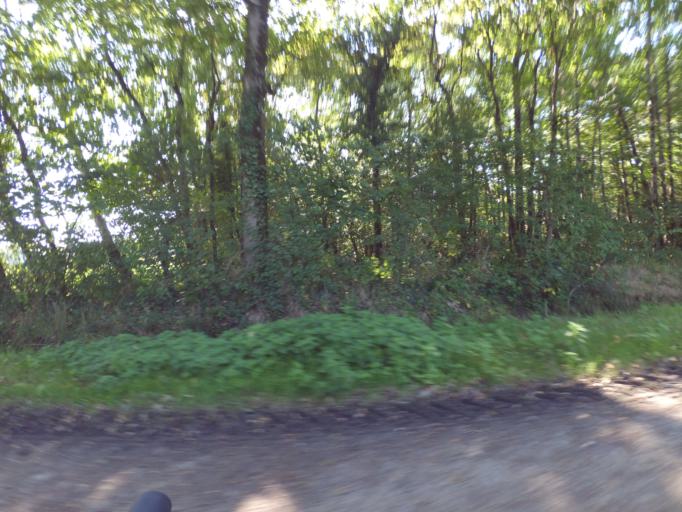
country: FR
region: Pays de la Loire
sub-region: Departement de la Loire-Atlantique
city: Chemere
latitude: 47.1084
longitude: -1.9130
